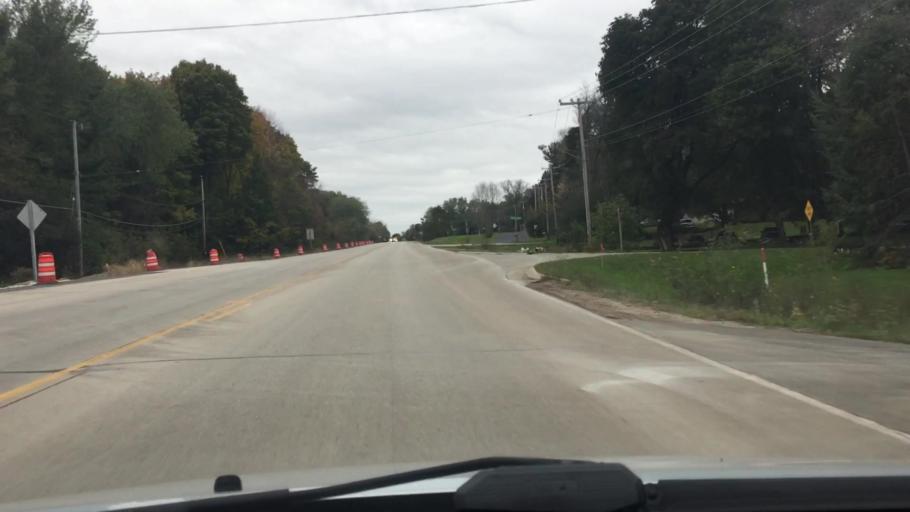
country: US
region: Wisconsin
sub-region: Waukesha County
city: Waukesha
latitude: 42.9786
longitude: -88.2791
